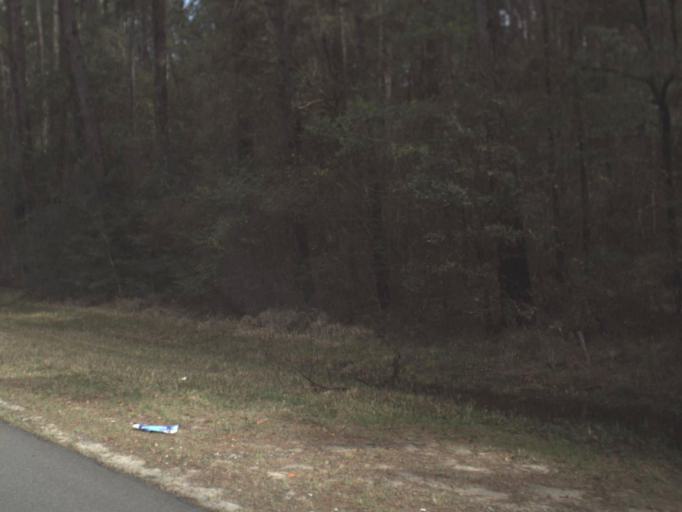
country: US
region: Florida
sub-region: Leon County
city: Woodville
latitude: 30.2976
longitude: -84.3491
